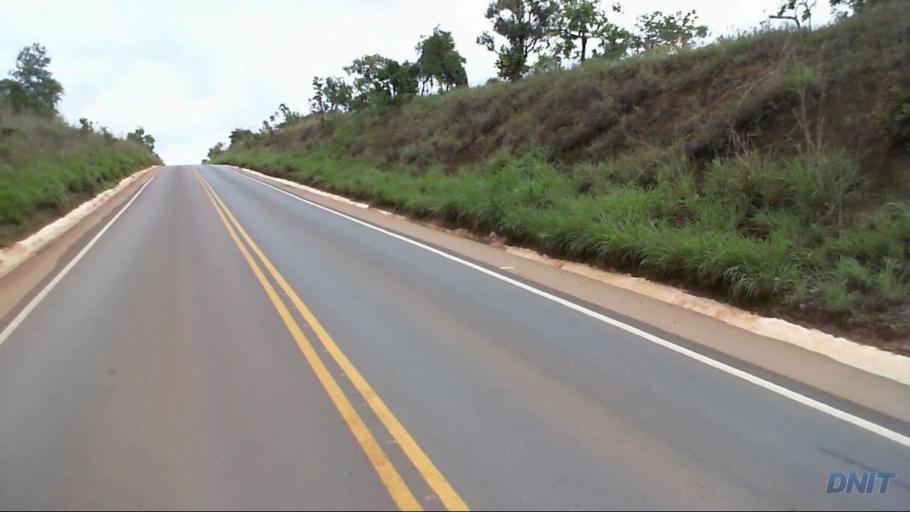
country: BR
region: Goias
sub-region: Padre Bernardo
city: Padre Bernardo
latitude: -15.3695
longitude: -48.2197
